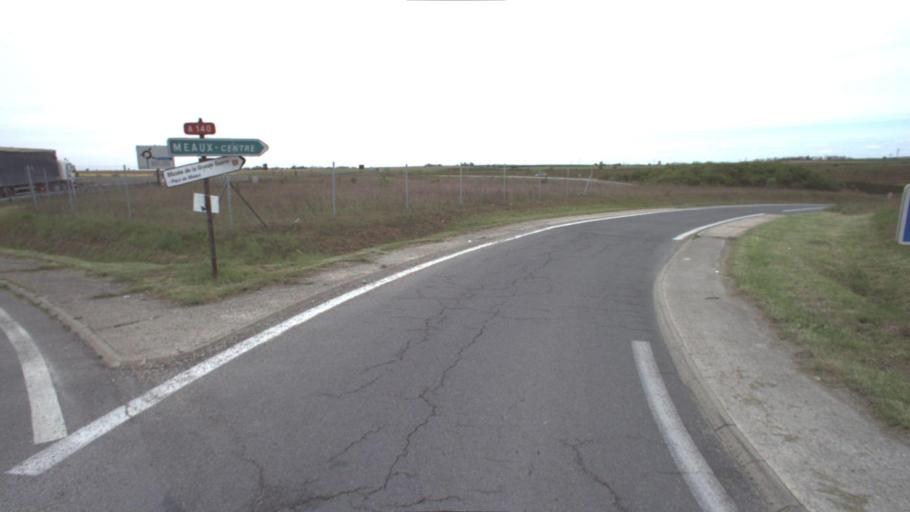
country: FR
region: Ile-de-France
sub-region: Departement de Seine-et-Marne
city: Villenoy
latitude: 48.9398
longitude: 2.8487
